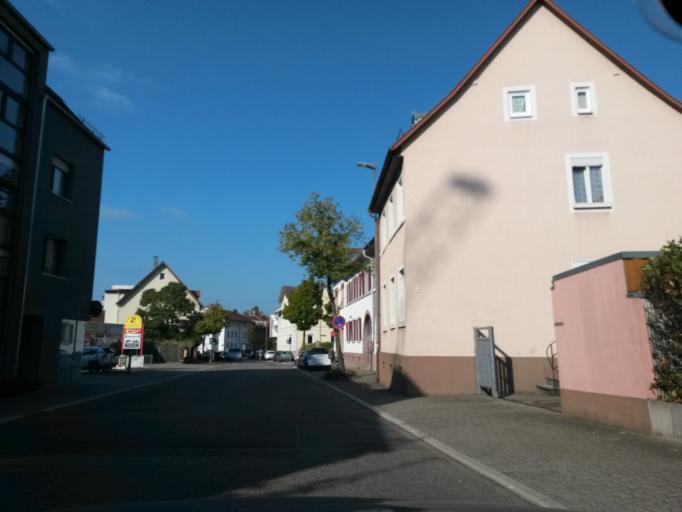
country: DE
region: Baden-Wuerttemberg
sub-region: Karlsruhe Region
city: Ettlingen
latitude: 48.9422
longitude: 8.4036
